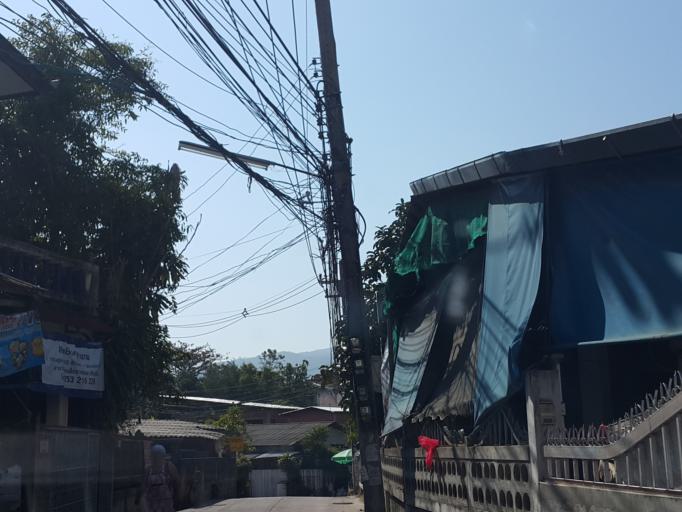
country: TH
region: Chiang Mai
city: Chiang Mai
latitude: 18.8091
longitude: 98.9702
